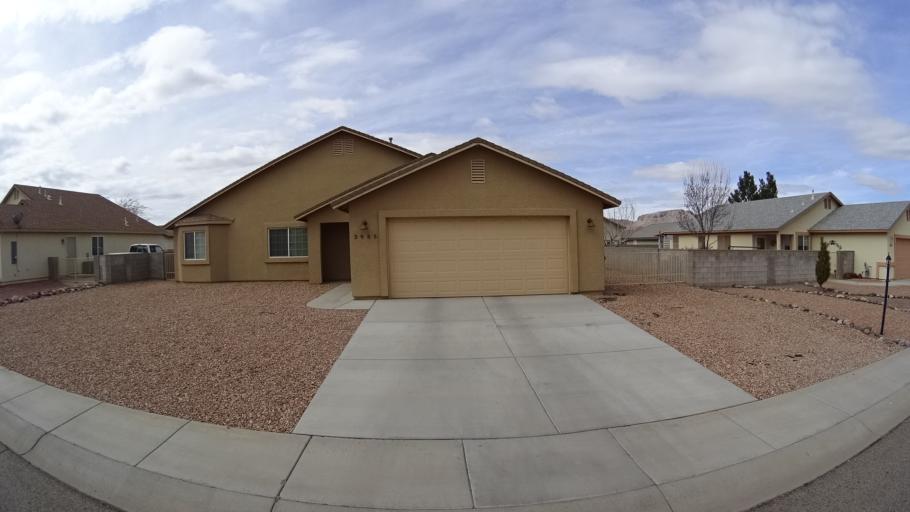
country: US
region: Arizona
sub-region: Mohave County
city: New Kingman-Butler
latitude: 35.2381
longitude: -113.9998
